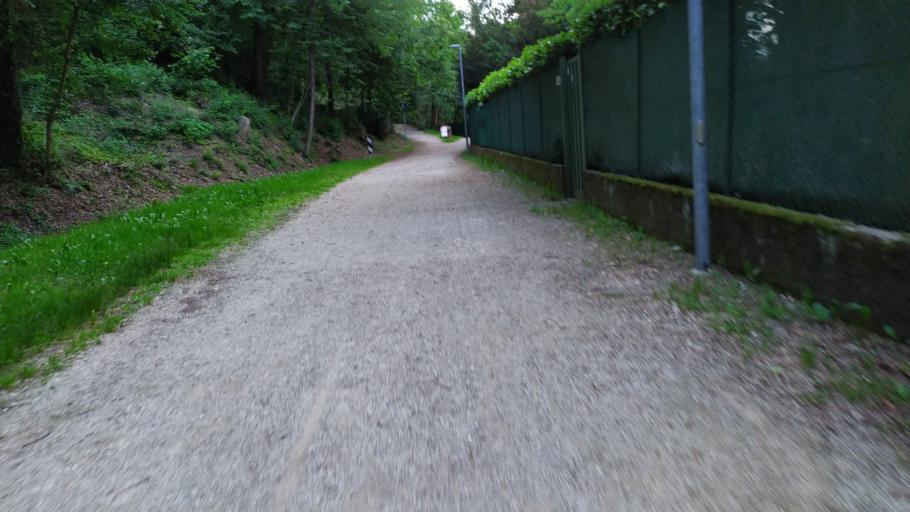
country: IT
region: Veneto
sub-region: Provincia di Vicenza
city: Malo
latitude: 45.6623
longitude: 11.3993
